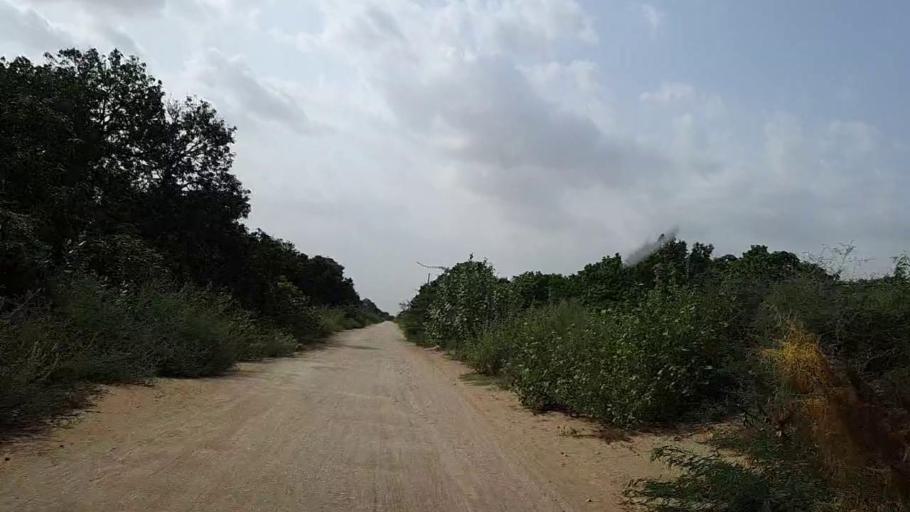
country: PK
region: Sindh
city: Kotri
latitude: 25.2424
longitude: 68.2636
